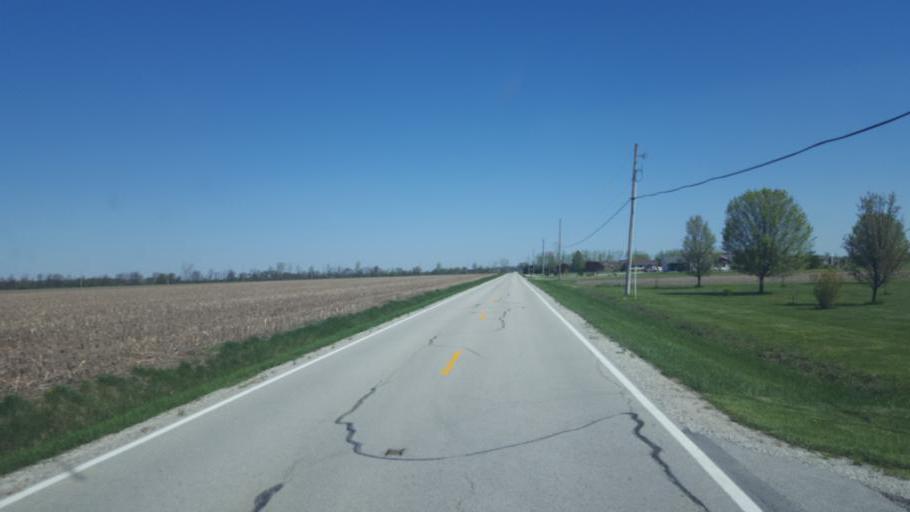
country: US
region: Ohio
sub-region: Sandusky County
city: Stony Prairie
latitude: 41.2937
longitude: -83.1974
